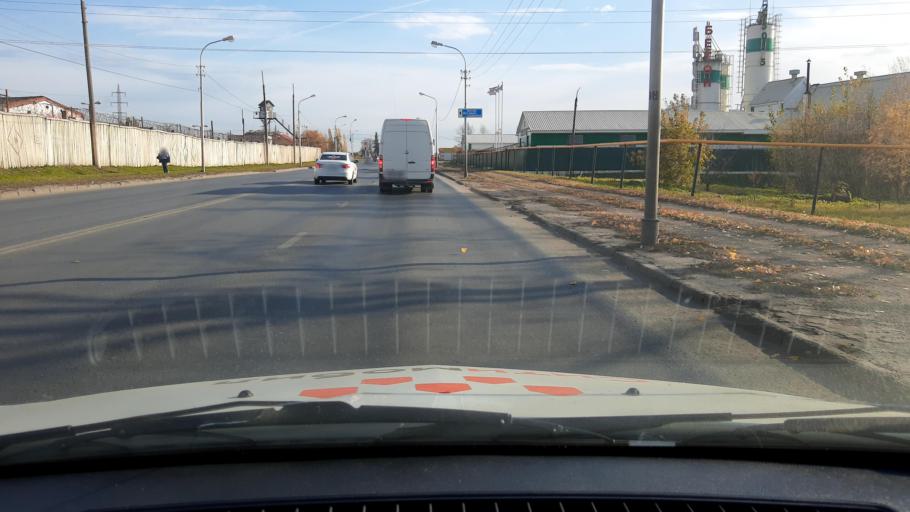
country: RU
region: Bashkortostan
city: Iglino
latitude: 54.7839
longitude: 56.2221
